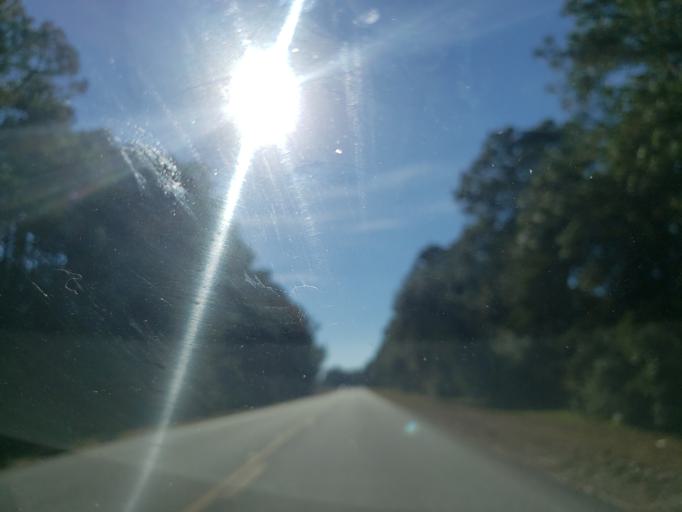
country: US
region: Georgia
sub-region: Glynn County
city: Country Club Estates
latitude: 31.2966
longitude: -81.4866
